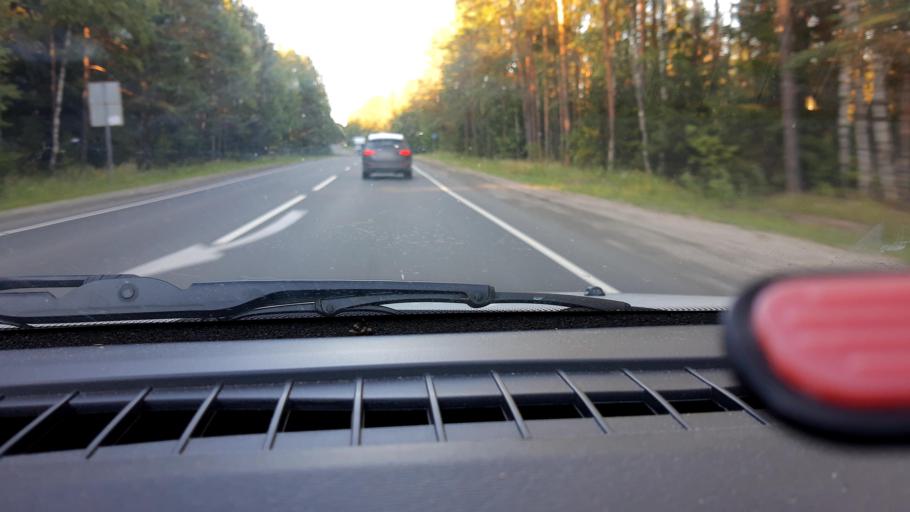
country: RU
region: Nizjnij Novgorod
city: Linda
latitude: 56.7153
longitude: 44.2692
